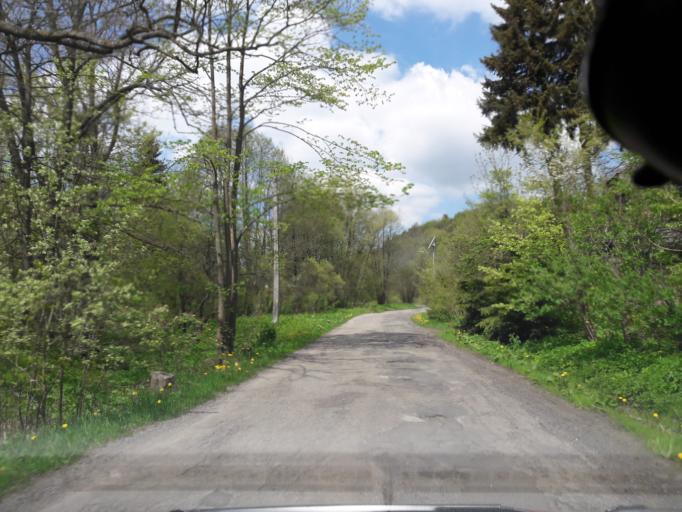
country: PL
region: Lower Silesian Voivodeship
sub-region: Powiat klodzki
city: Duszniki-Zdroj
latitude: 50.4387
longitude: 16.3552
